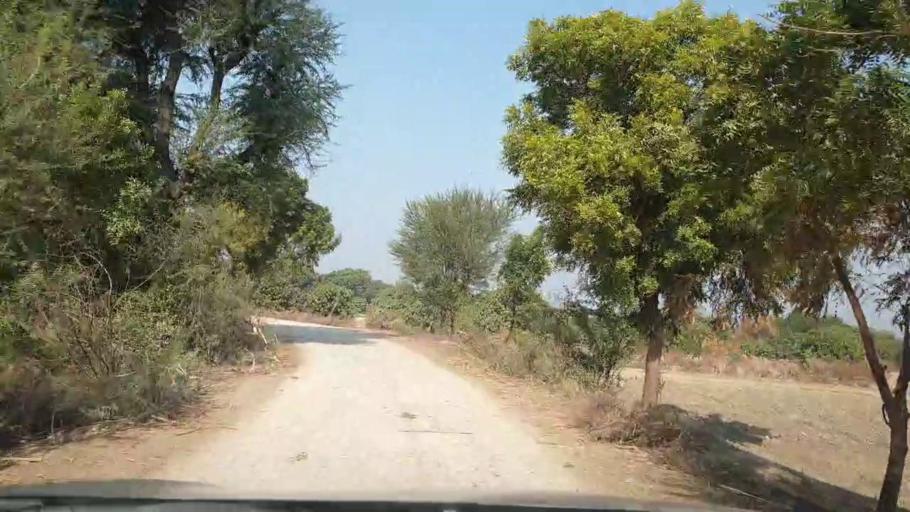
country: PK
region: Sindh
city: Tando Allahyar
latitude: 25.5308
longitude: 68.7813
